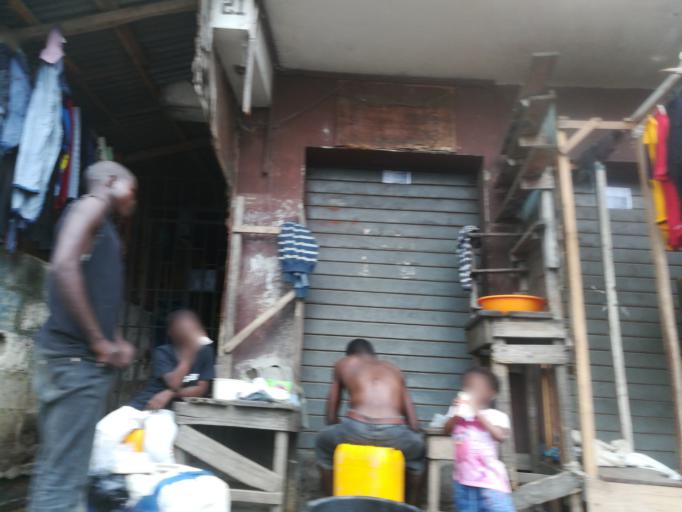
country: NG
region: Lagos
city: Lagos
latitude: 6.4588
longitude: 3.3911
